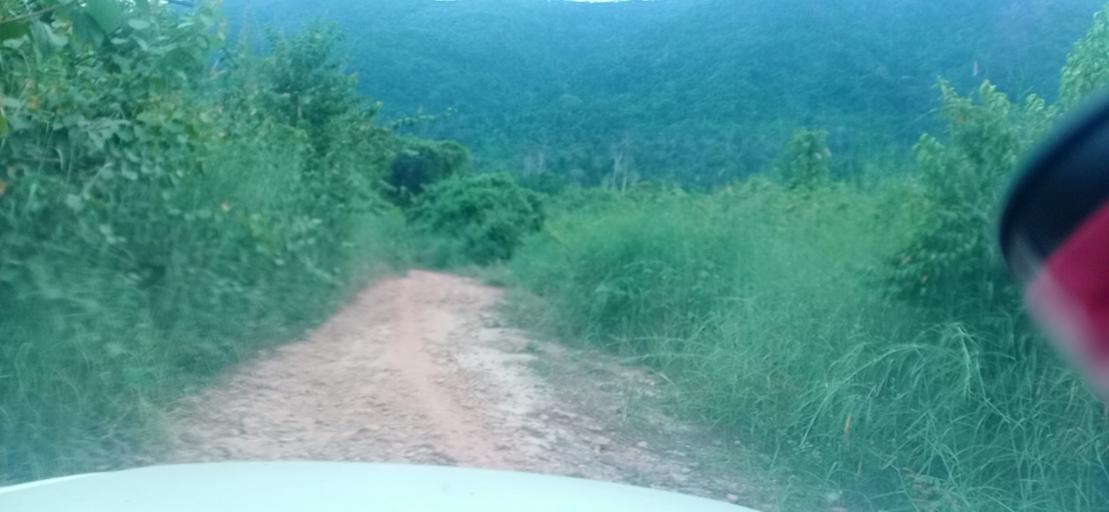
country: TH
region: Changwat Bueng Kan
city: Pak Khat
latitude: 18.5613
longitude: 103.2915
